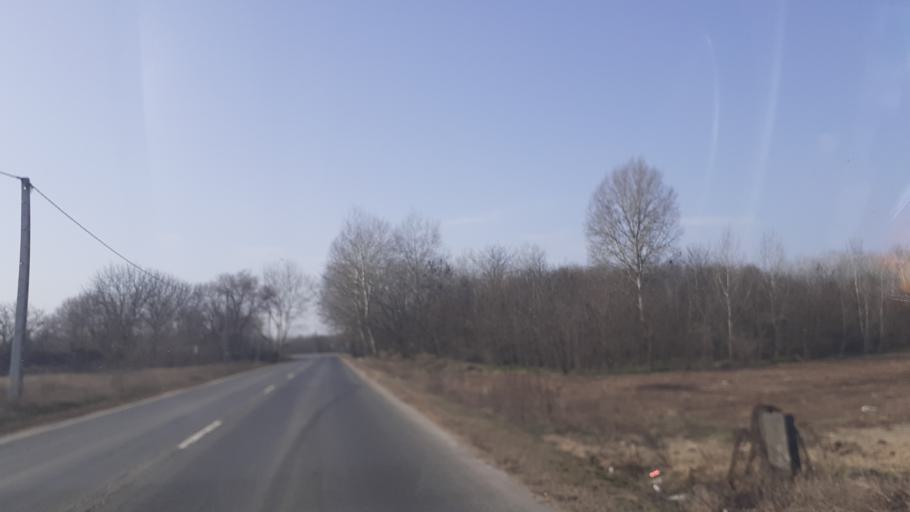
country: HU
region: Pest
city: Orkeny
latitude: 47.1372
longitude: 19.4467
